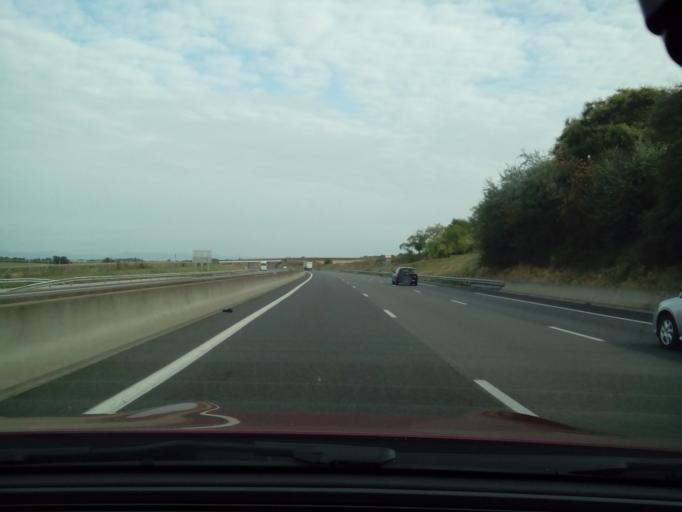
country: FR
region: Rhone-Alpes
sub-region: Departement du Rhone
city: Montanay
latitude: 45.8906
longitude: 4.8921
